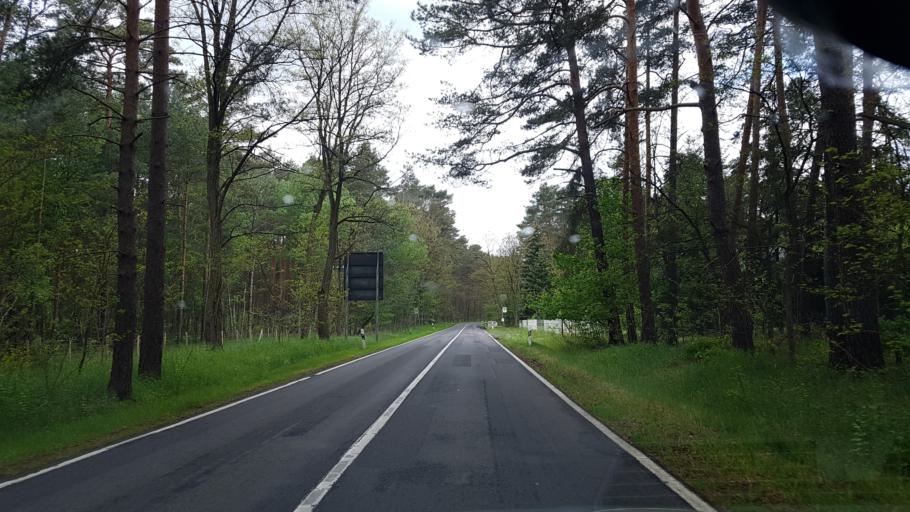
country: DE
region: Brandenburg
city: Jamlitz
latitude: 52.0741
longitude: 14.4003
